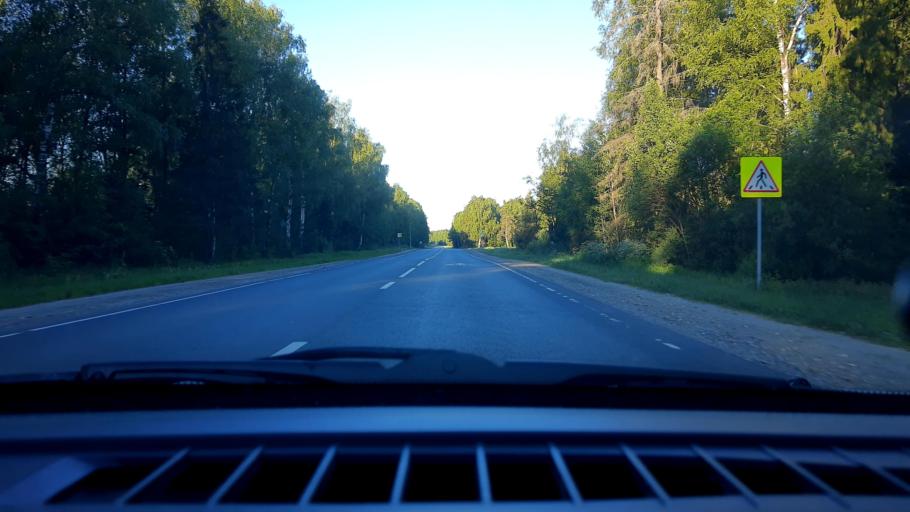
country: RU
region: Nizjnij Novgorod
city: Linda
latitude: 56.6279
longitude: 44.0864
